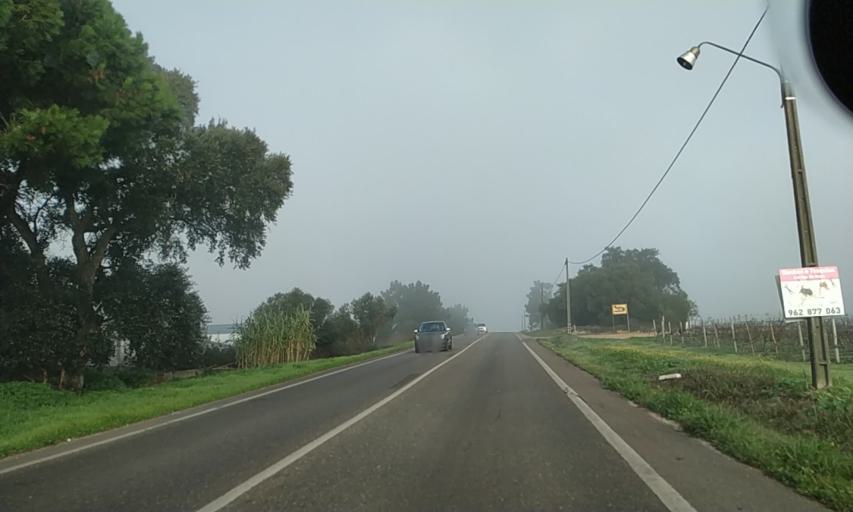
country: PT
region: Setubal
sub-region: Palmela
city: Pinhal Novo
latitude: 38.6082
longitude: -8.9082
